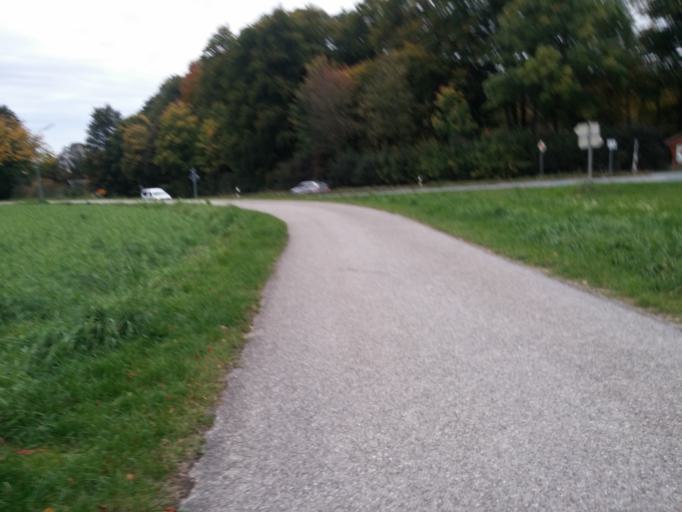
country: DE
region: Bavaria
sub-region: Upper Bavaria
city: Kirchseeon
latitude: 48.0737
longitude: 11.8926
